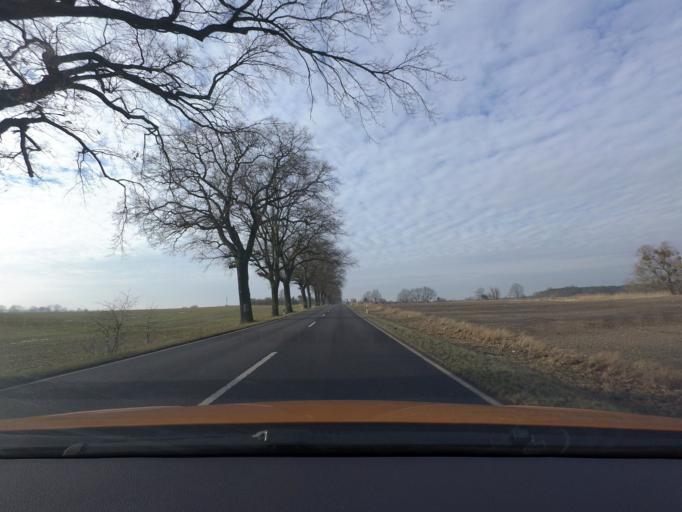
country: DE
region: Brandenburg
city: Gransee
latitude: 52.8985
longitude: 13.2079
